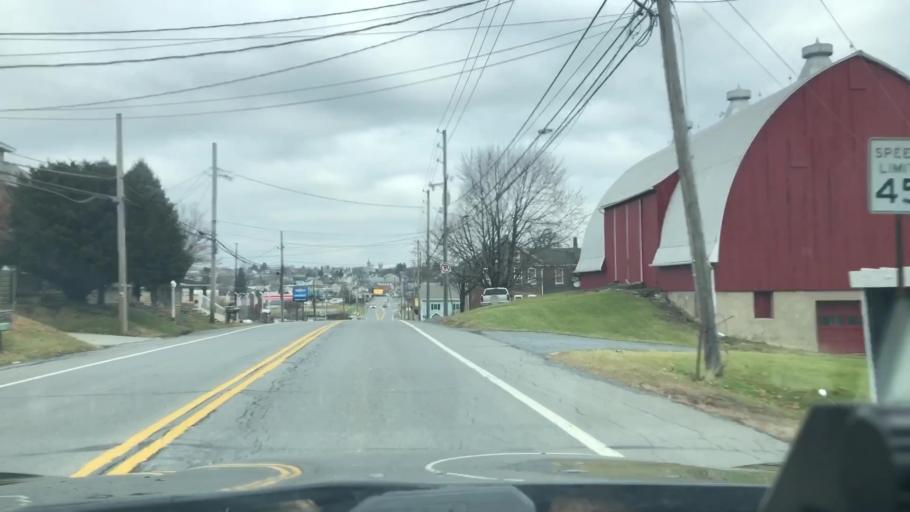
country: US
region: Pennsylvania
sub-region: Northampton County
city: Nazareth
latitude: 40.7269
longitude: -75.3160
